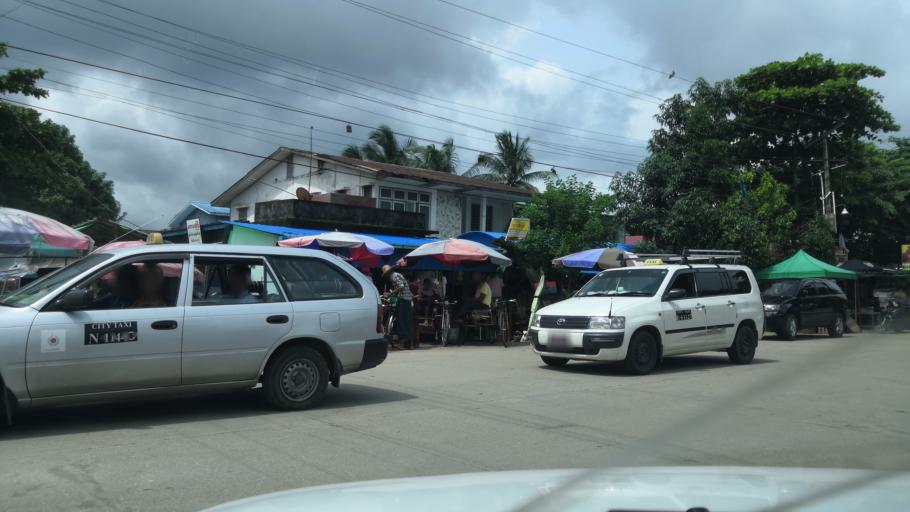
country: MM
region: Yangon
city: Yangon
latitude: 16.8752
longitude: 96.1827
